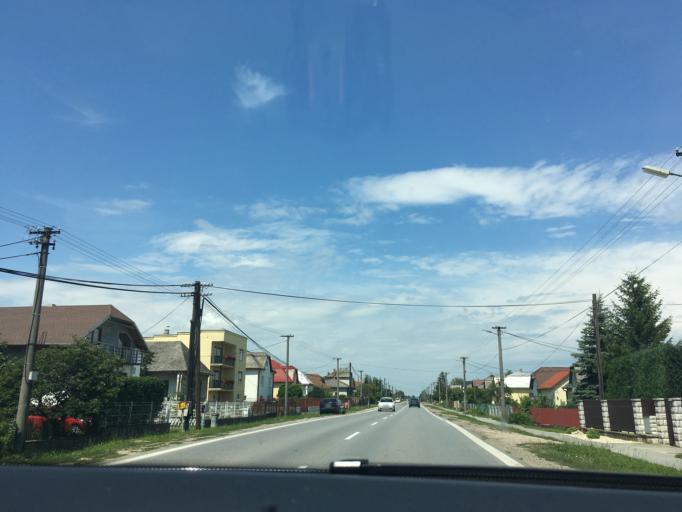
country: SK
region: Kosicky
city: Secovce
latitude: 48.7897
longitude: 21.6811
